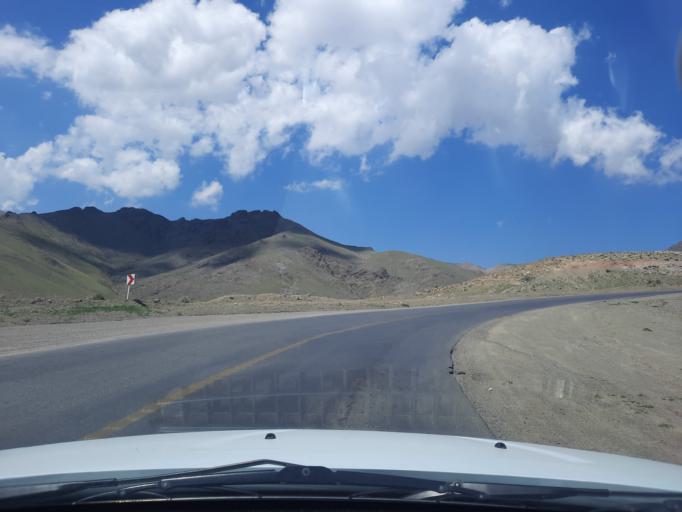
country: IR
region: Qazvin
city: Qazvin
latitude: 36.3552
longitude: 50.1868
